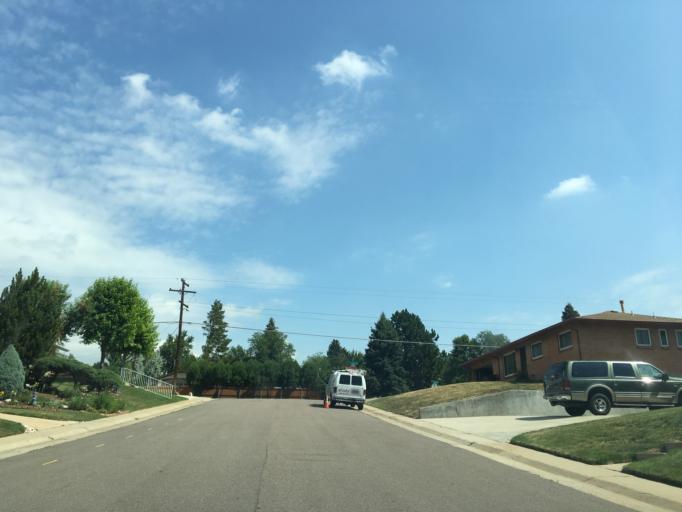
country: US
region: Colorado
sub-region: Arapahoe County
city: Sheridan
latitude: 39.6671
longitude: -105.0458
